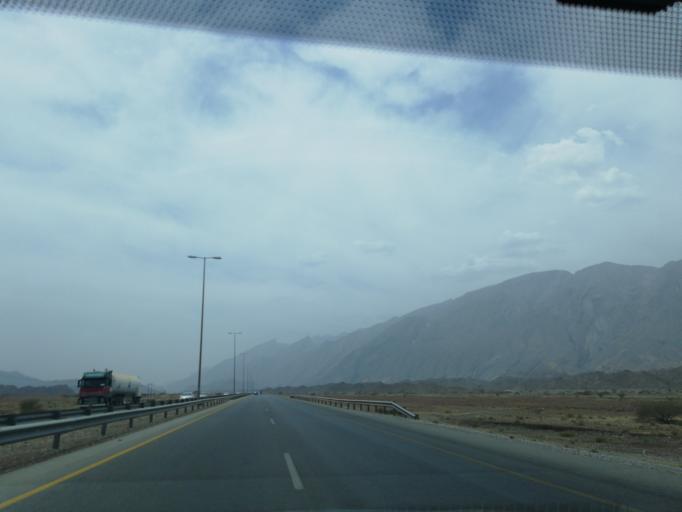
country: OM
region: Muhafazat ad Dakhiliyah
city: Sufalat Sama'il
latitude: 23.2369
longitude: 57.9096
